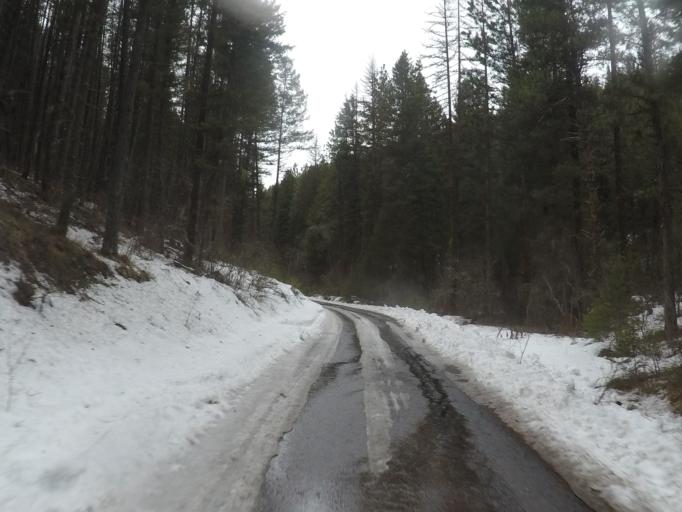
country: US
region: Montana
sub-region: Missoula County
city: East Missoula
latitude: 46.9288
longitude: -113.9676
